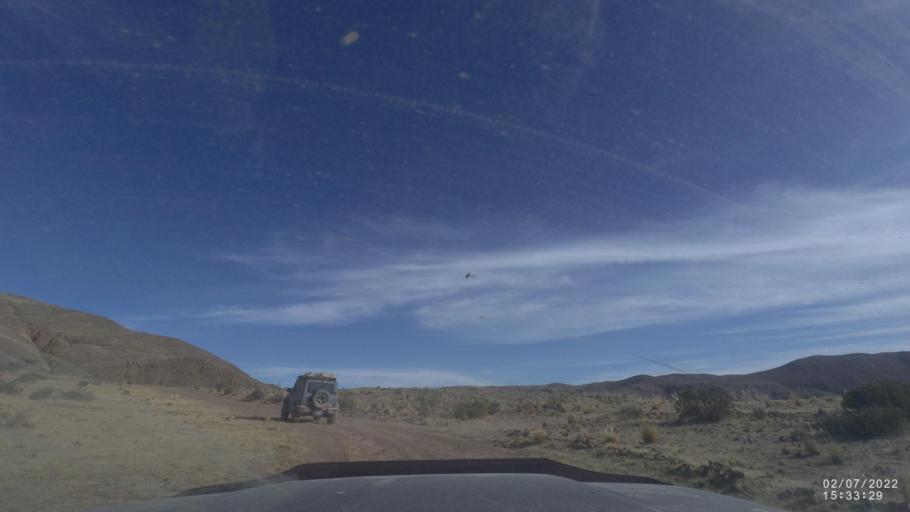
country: BO
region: Cochabamba
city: Irpa Irpa
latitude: -17.8865
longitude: -66.4140
